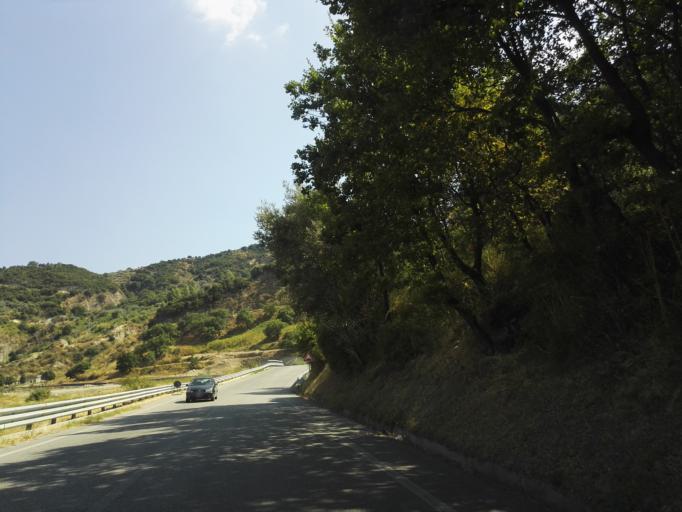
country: IT
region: Calabria
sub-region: Provincia di Reggio Calabria
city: Stilo
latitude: 38.4687
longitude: 16.4851
